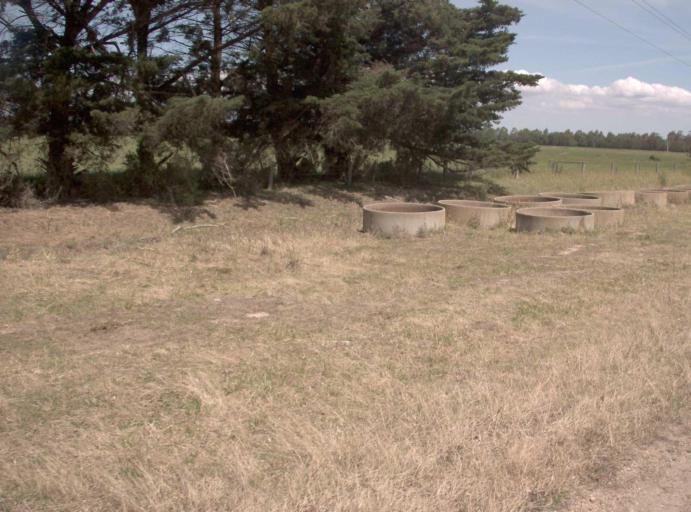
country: AU
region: Victoria
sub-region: Wellington
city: Heyfield
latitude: -37.9997
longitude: 146.8845
